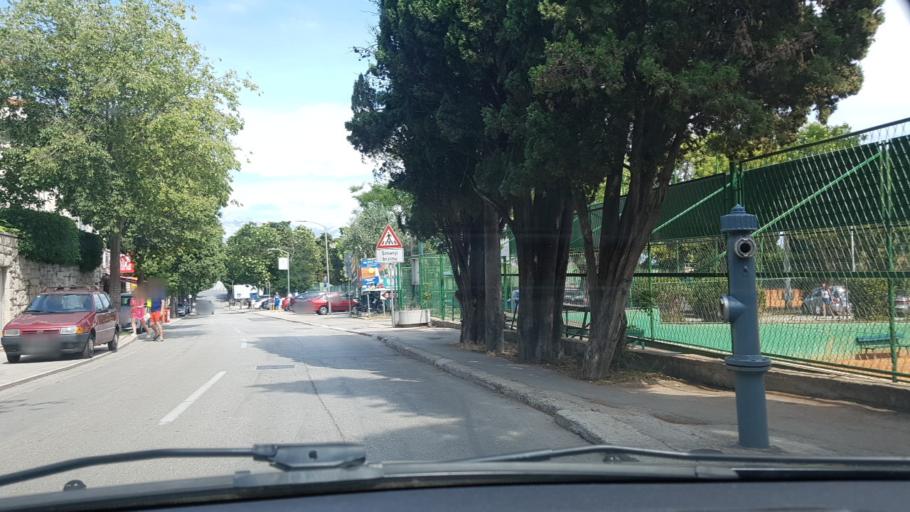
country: HR
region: Splitsko-Dalmatinska
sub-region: Grad Split
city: Split
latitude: 43.5013
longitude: 16.4546
